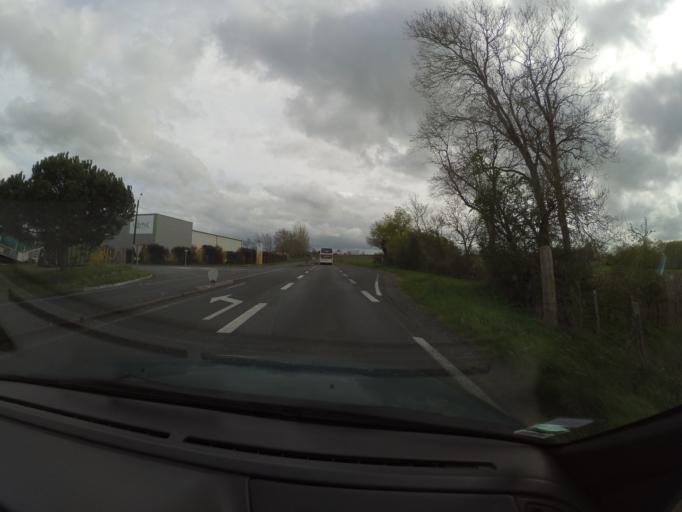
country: FR
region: Pays de la Loire
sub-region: Departement de Maine-et-Loire
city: Lire
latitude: 47.3206
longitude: -1.1647
